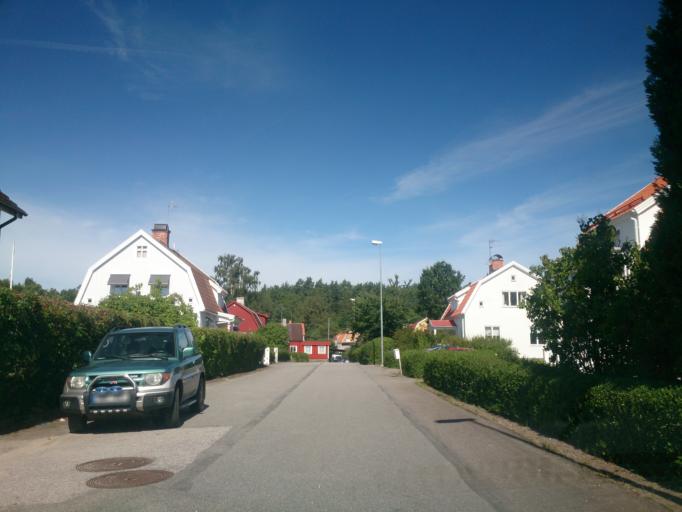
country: SE
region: OEstergoetland
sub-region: Atvidabergs Kommun
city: Atvidaberg
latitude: 58.2046
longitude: 16.0038
